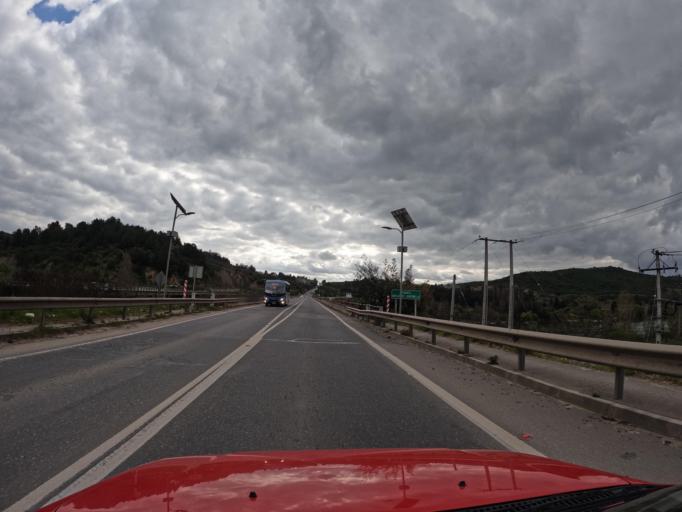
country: CL
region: Maule
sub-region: Provincia de Linares
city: San Javier
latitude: -35.6211
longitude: -71.7673
